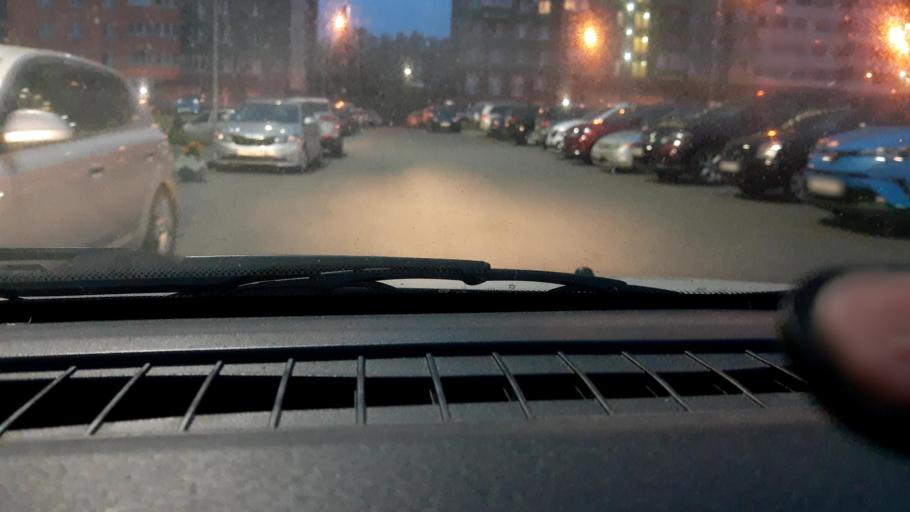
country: RU
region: Nizjnij Novgorod
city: Afonino
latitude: 56.2779
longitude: 44.0855
